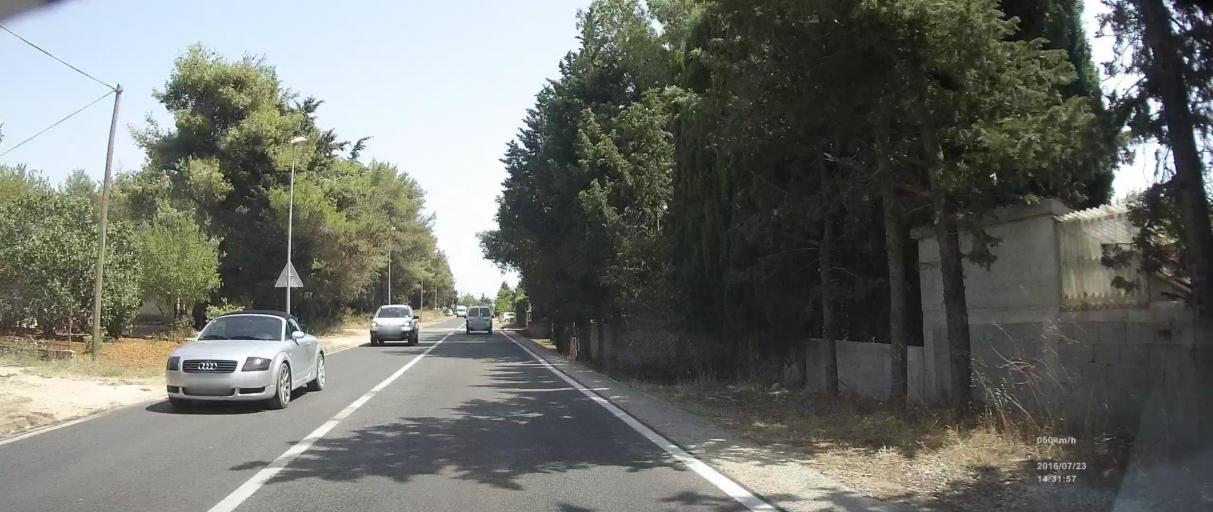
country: HR
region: Zadarska
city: Turanj
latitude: 43.9722
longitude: 15.4038
